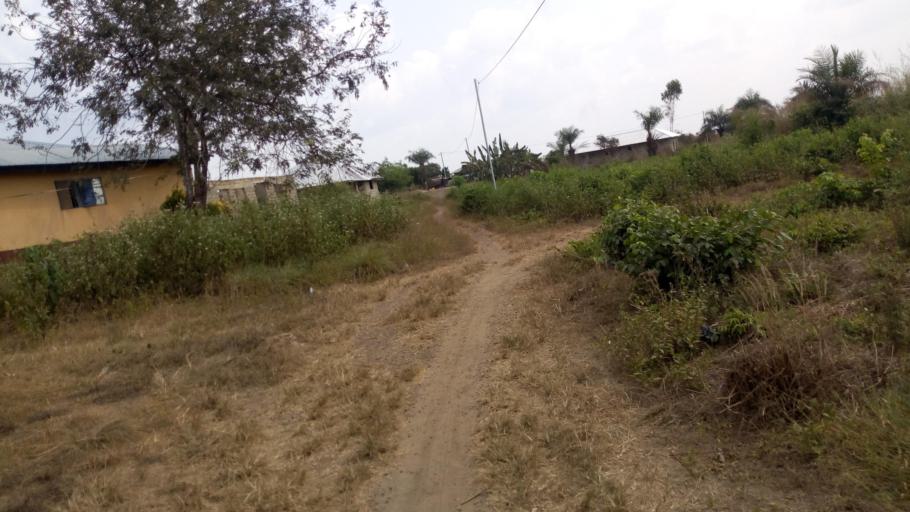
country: SL
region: Southern Province
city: Mogbwemo
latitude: 7.7862
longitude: -12.3088
